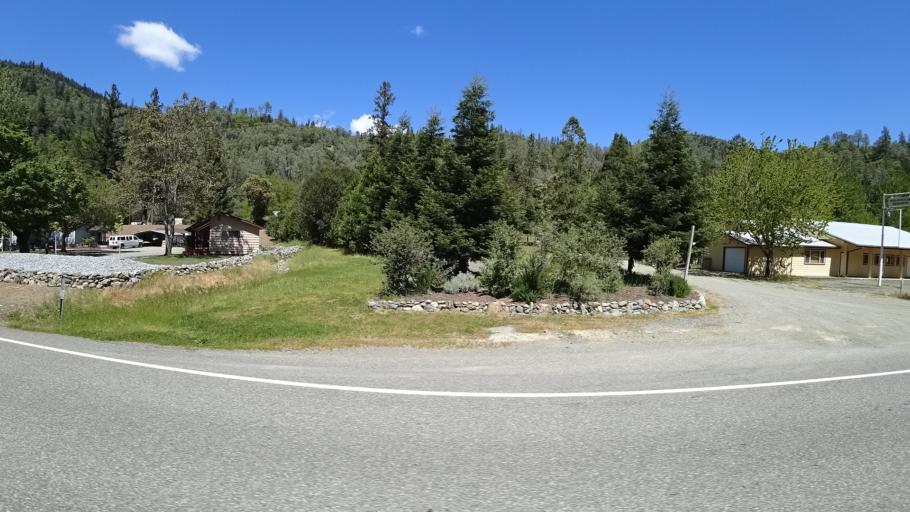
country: US
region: California
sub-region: Trinity County
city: Hayfork
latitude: 40.7396
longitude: -123.2079
